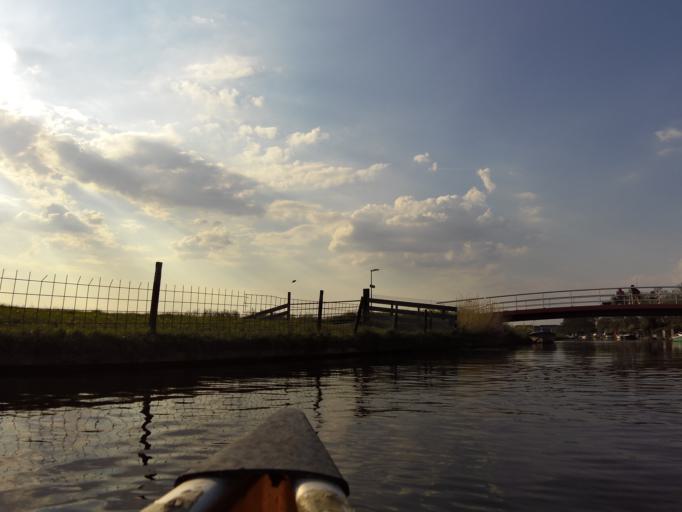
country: NL
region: South Holland
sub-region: Gemeente Voorschoten
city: Voorschoten
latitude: 52.1432
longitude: 4.4493
